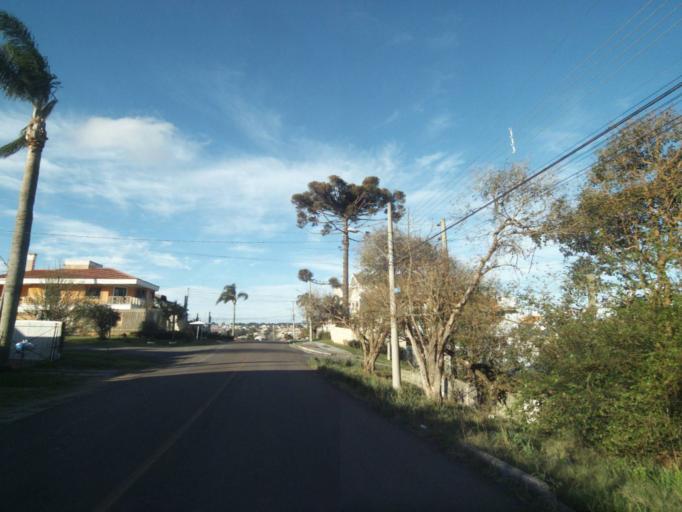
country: BR
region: Parana
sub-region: Curitiba
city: Curitiba
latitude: -25.3835
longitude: -49.2528
